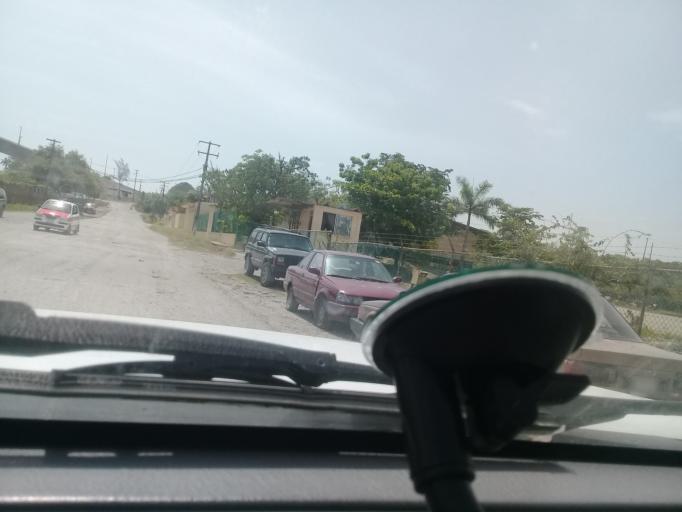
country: MX
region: Veracruz
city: Anahuac
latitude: 22.2253
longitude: -97.8356
